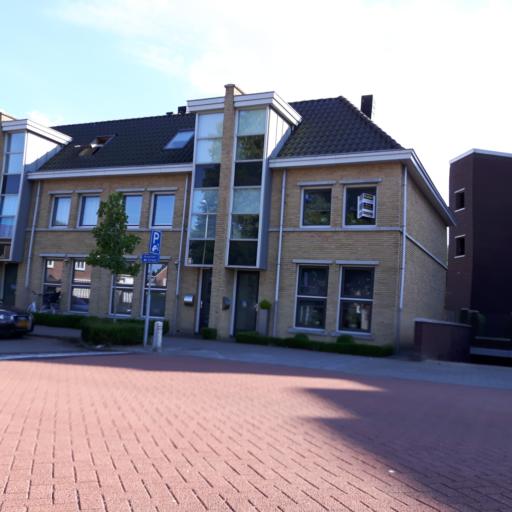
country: NL
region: Zeeland
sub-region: Gemeente Goes
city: Goes
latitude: 51.5044
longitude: 3.8941
